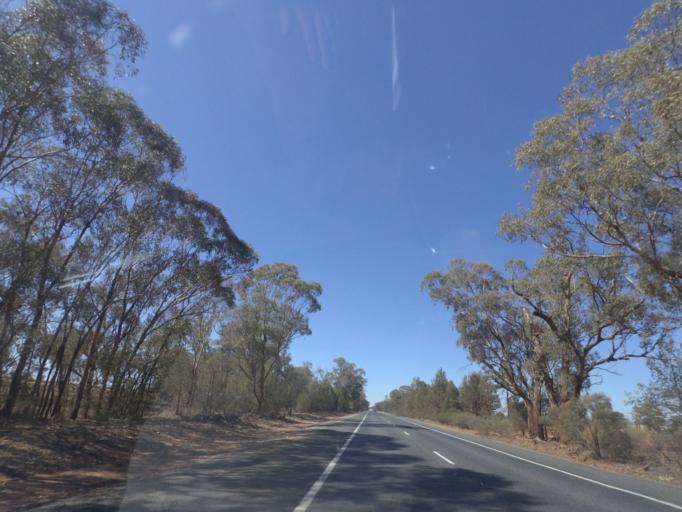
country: AU
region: New South Wales
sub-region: Bland
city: West Wyalong
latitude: -34.2122
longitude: 147.1085
